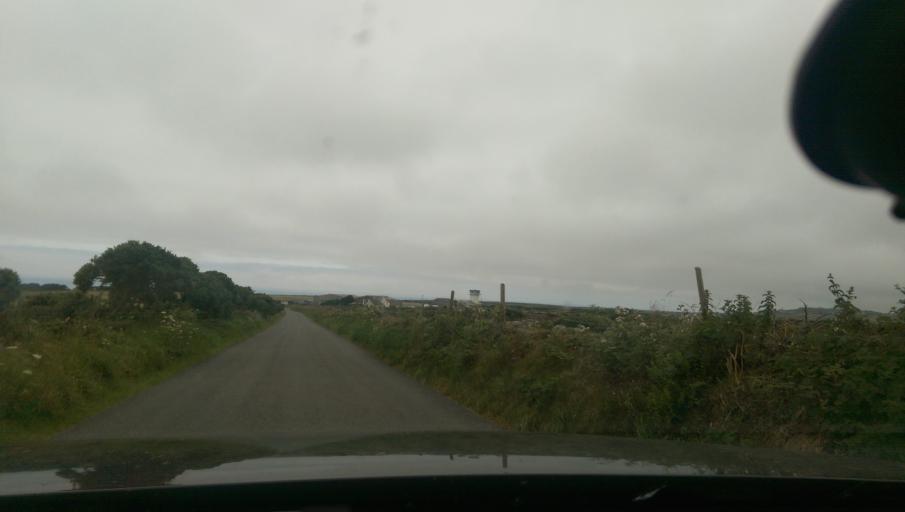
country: GB
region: England
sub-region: Cornwall
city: Saint Just
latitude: 50.0998
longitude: -5.6619
